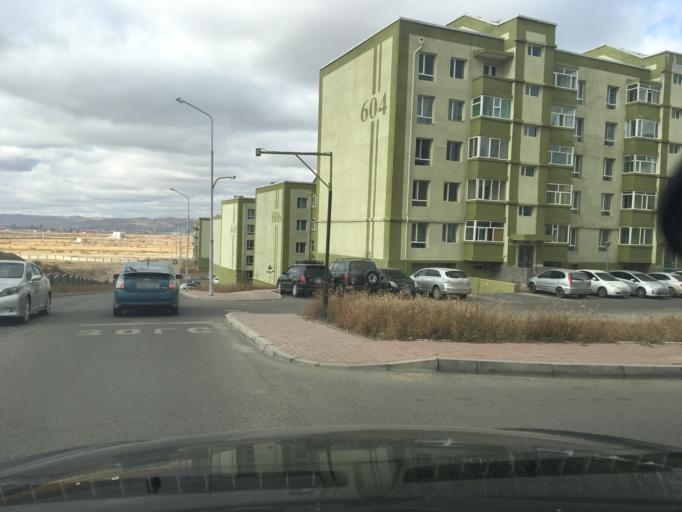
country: MN
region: Ulaanbaatar
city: Ulaanbaatar
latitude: 47.8769
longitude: 106.8480
